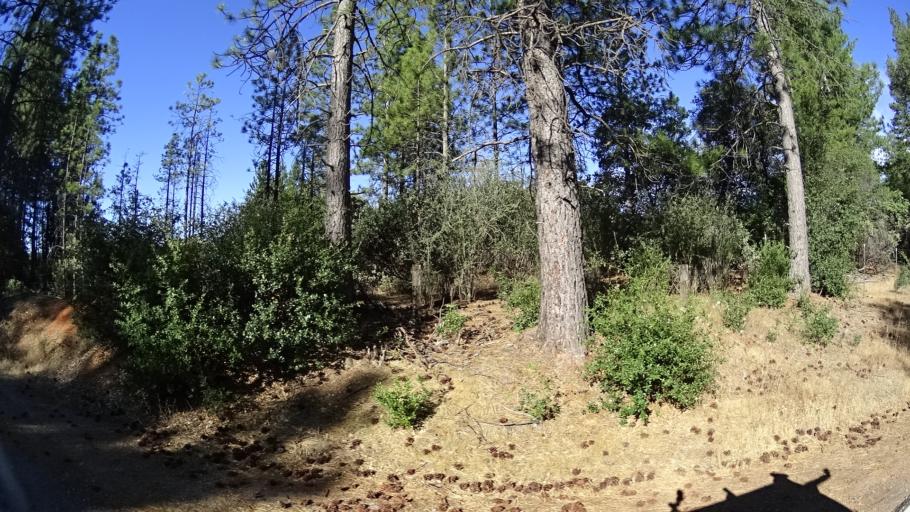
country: US
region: California
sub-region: Amador County
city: Pioneer
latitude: 38.3802
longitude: -120.5271
